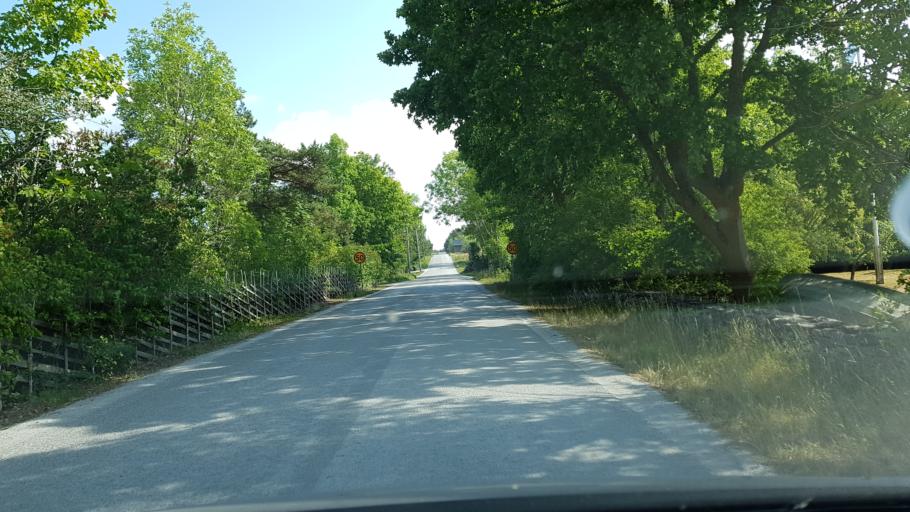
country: SE
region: Gotland
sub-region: Gotland
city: Visby
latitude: 57.8233
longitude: 18.5153
